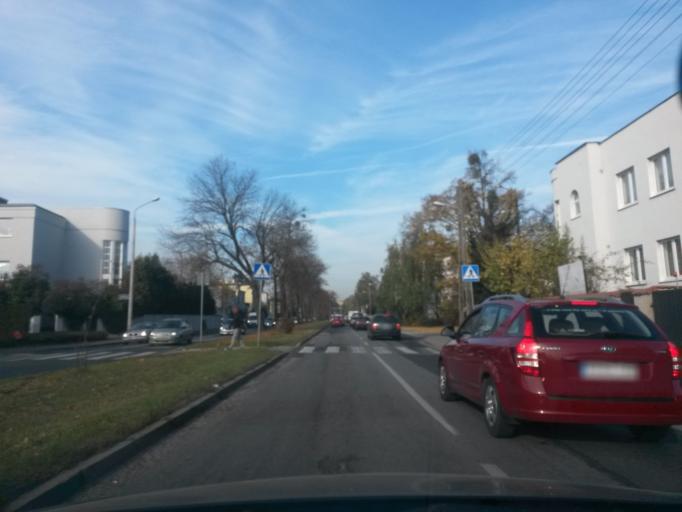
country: PL
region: Greater Poland Voivodeship
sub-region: Poznan
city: Poznan
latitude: 52.3968
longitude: 16.8800
